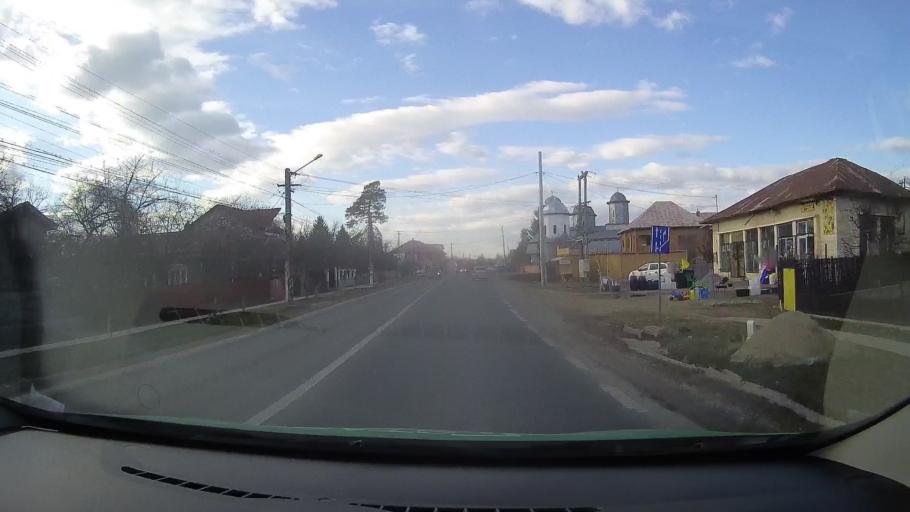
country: RO
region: Dambovita
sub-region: Comuna Ulmi
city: Ulmi
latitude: 44.8945
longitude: 25.5022
